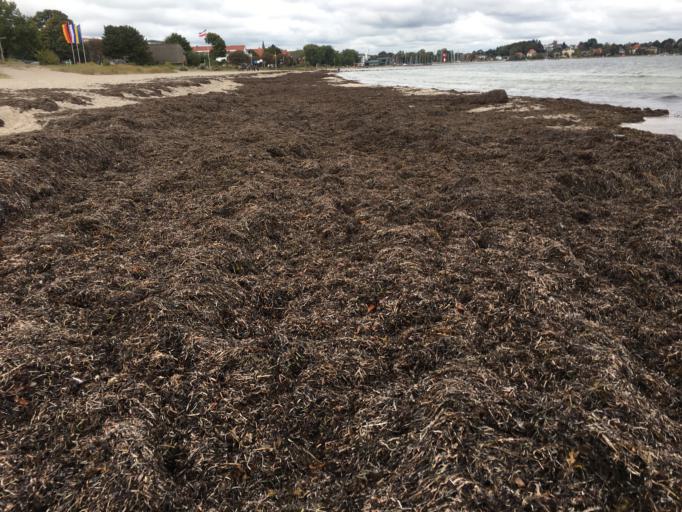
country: DE
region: Schleswig-Holstein
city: Eckernforde
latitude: 54.4669
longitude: 9.8408
